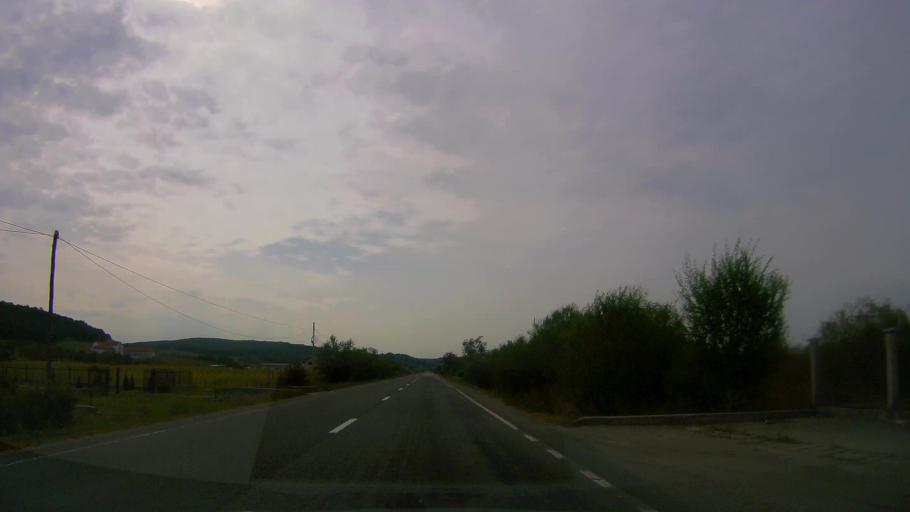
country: RO
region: Salaj
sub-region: Comuna Romanasi
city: Romanasi
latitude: 47.1043
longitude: 23.1865
